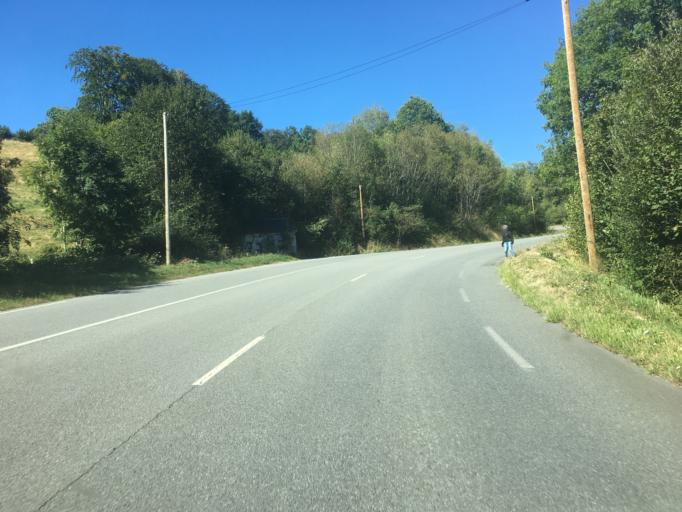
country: FR
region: Limousin
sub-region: Departement de la Correze
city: Bort-les-Orgues
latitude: 45.4100
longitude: 2.4921
